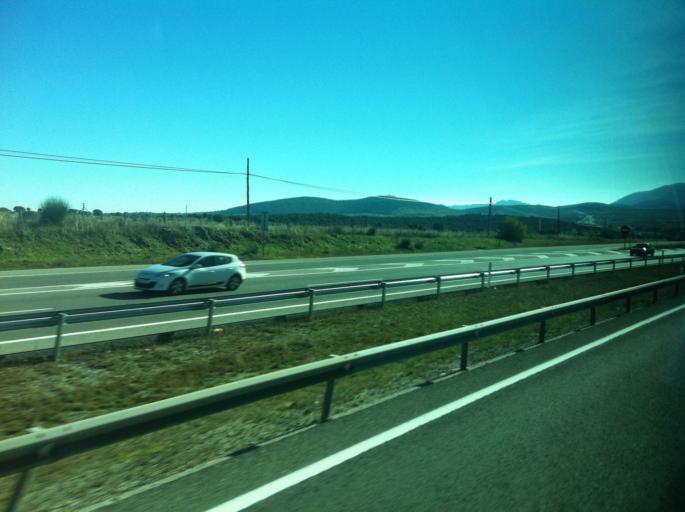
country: ES
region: Madrid
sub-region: Provincia de Madrid
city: Gascones
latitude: 41.0139
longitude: -3.6302
